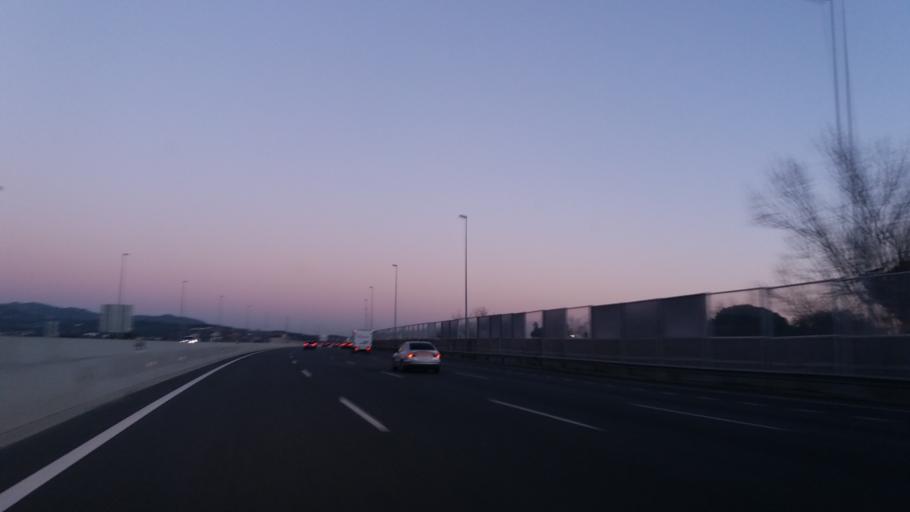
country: ES
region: Madrid
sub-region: Provincia de Madrid
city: Alpedrete
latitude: 40.6422
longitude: -4.0274
